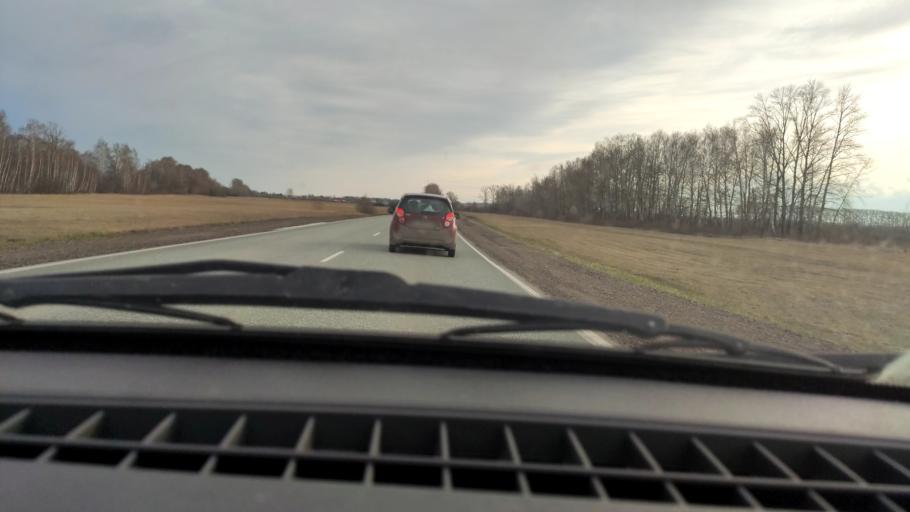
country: RU
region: Bashkortostan
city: Chishmy
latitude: 54.4095
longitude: 55.2209
